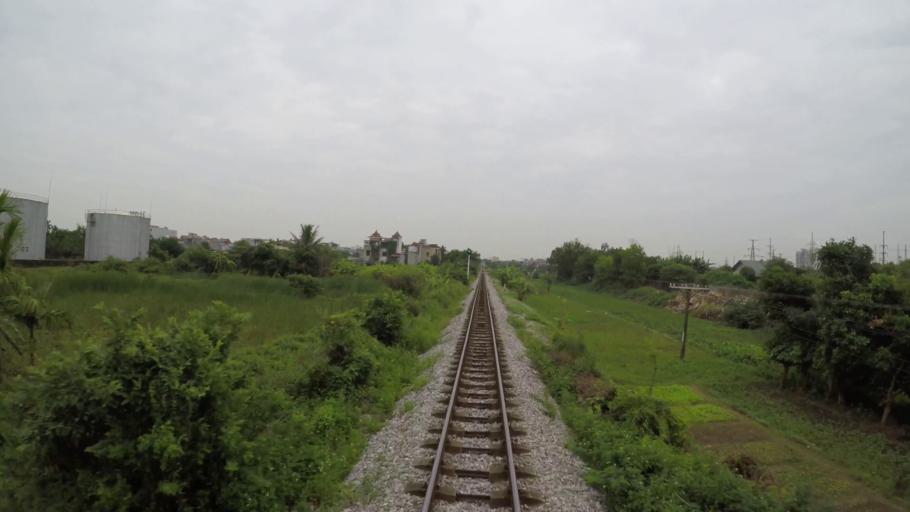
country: VN
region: Hai Phong
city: An Duong
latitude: 20.8887
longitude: 106.5970
